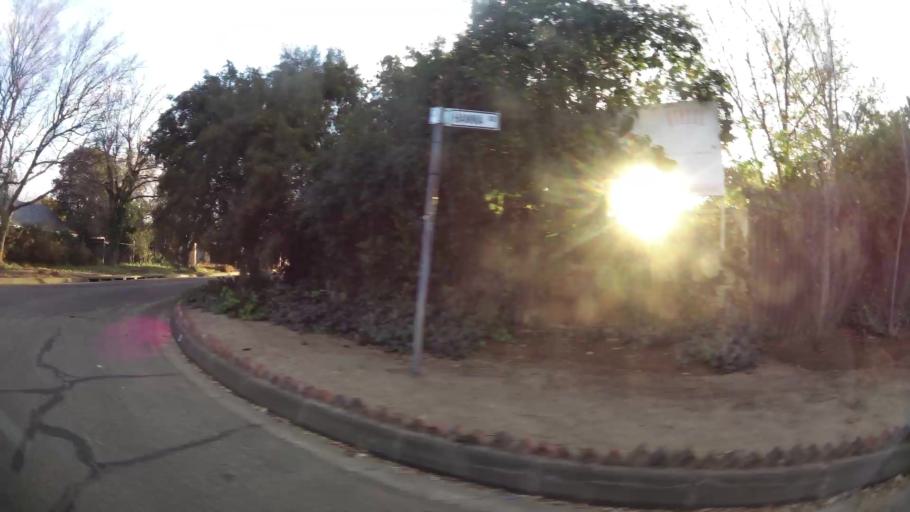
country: ZA
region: Orange Free State
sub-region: Mangaung Metropolitan Municipality
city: Bloemfontein
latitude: -29.1358
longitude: 26.1884
